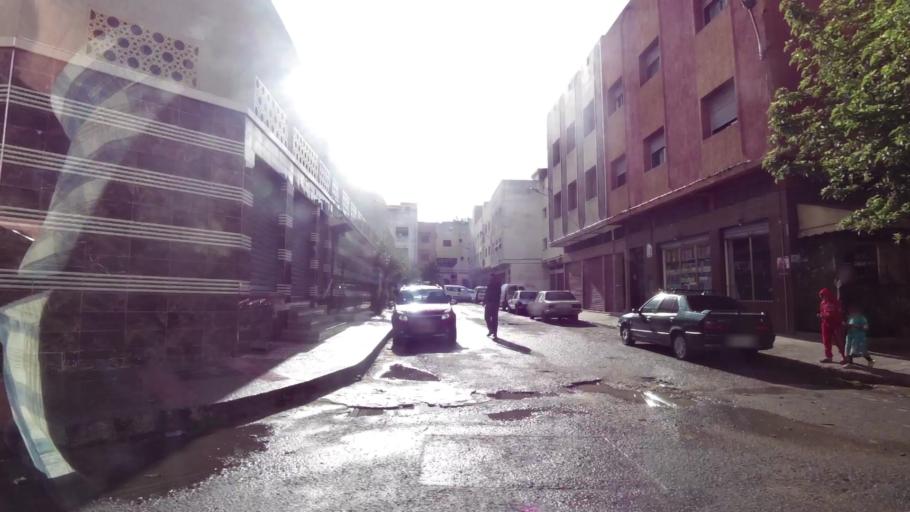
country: MA
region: Grand Casablanca
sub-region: Casablanca
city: Casablanca
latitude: 33.5580
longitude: -7.6857
